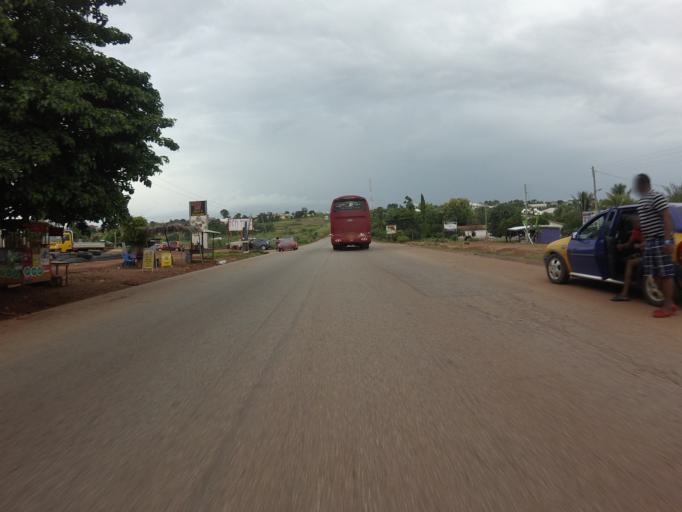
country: GH
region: Ashanti
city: Konongo
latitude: 6.6174
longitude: -1.1841
